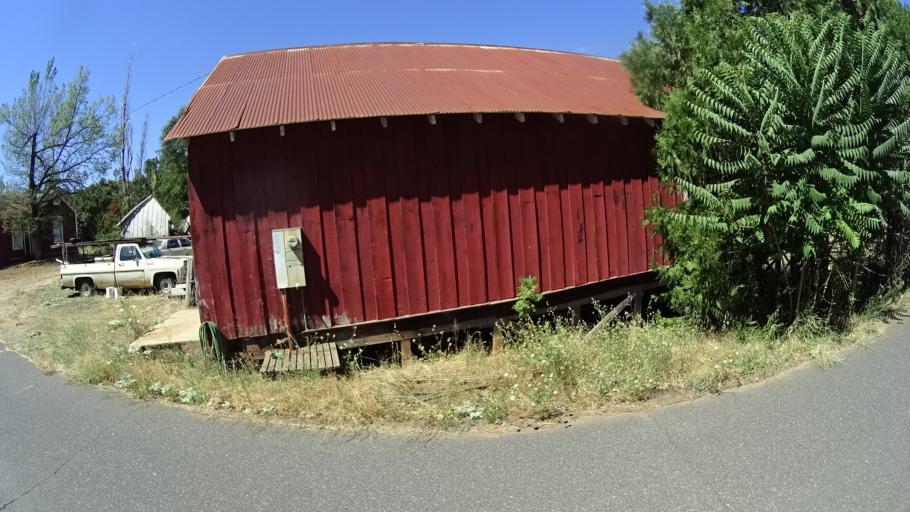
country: US
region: California
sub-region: Calaveras County
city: Angels Camp
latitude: 38.0735
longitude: -120.5355
